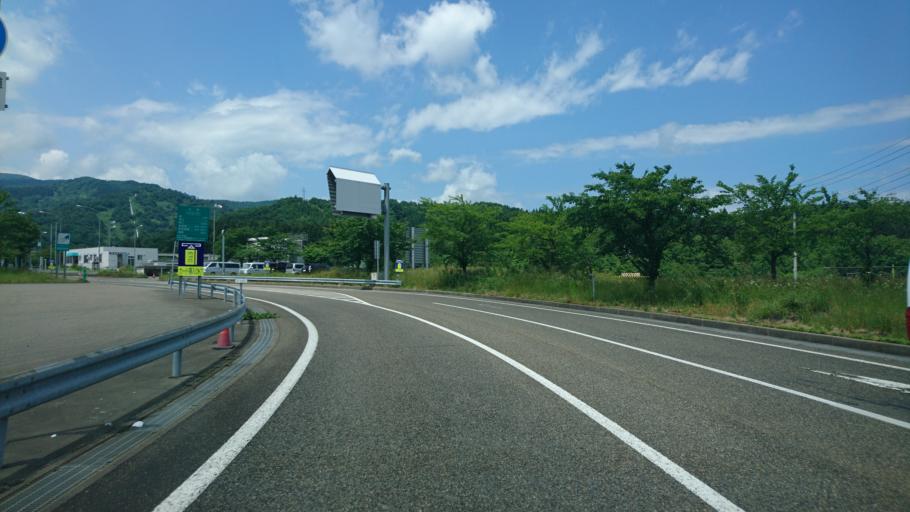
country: JP
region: Niigata
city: Joetsu
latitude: 37.0909
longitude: 138.2294
